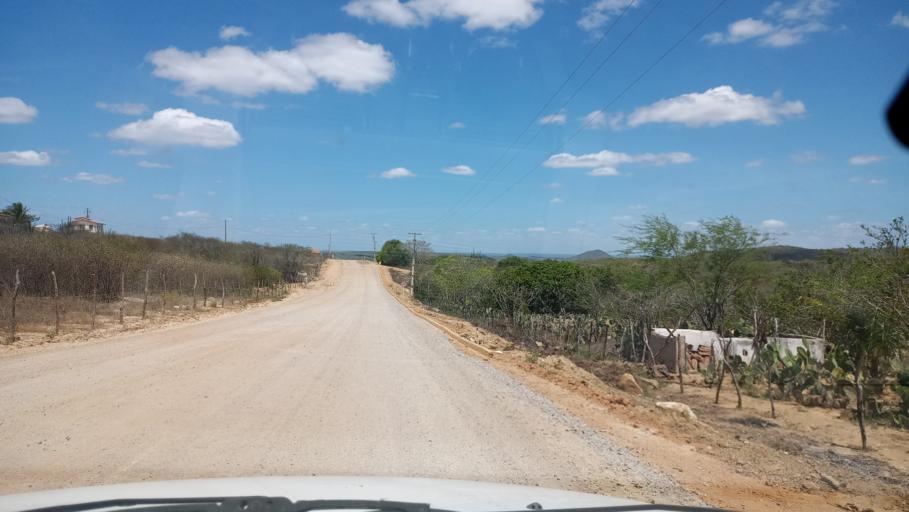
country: BR
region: Rio Grande do Norte
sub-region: Sao Paulo Do Potengi
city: Sao Paulo do Potengi
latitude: -5.7754
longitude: -35.9139
